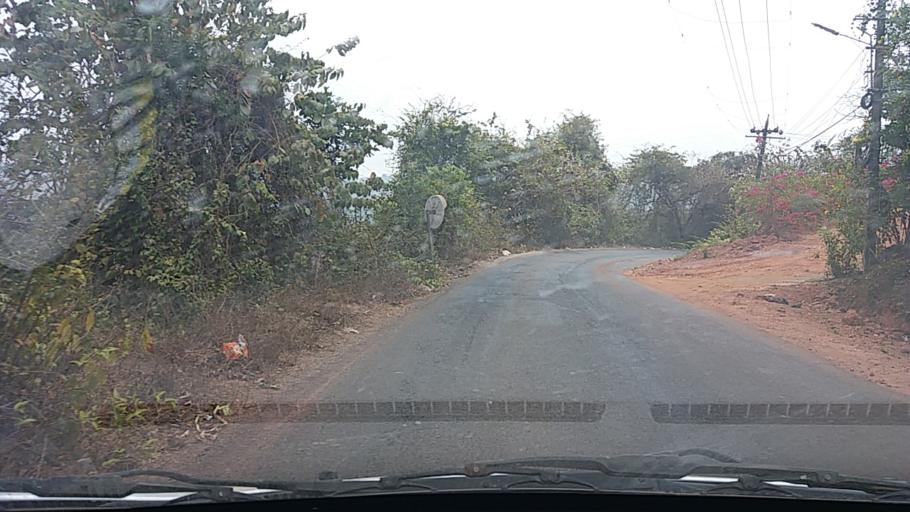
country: IN
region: Goa
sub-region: North Goa
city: Saligao
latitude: 15.5333
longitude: 73.7990
